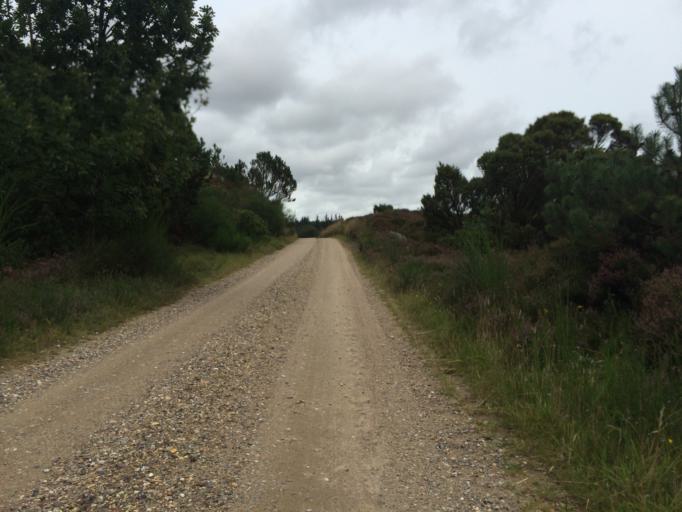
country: DK
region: Central Jutland
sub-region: Holstebro Kommune
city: Ulfborg
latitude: 56.2197
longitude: 8.3983
